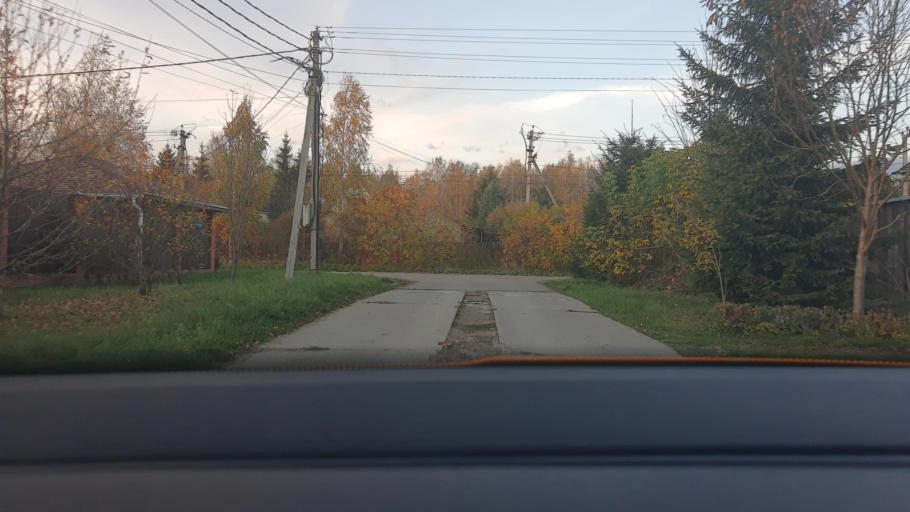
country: RU
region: Moskovskaya
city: Sheremet'yevskiy
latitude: 56.0028
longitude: 37.5273
